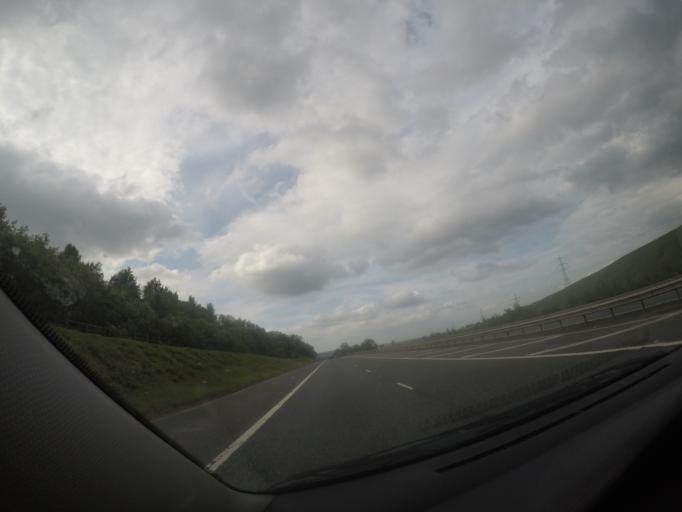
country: GB
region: Scotland
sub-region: South Lanarkshire
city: Douglas
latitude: 55.5625
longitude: -3.8049
